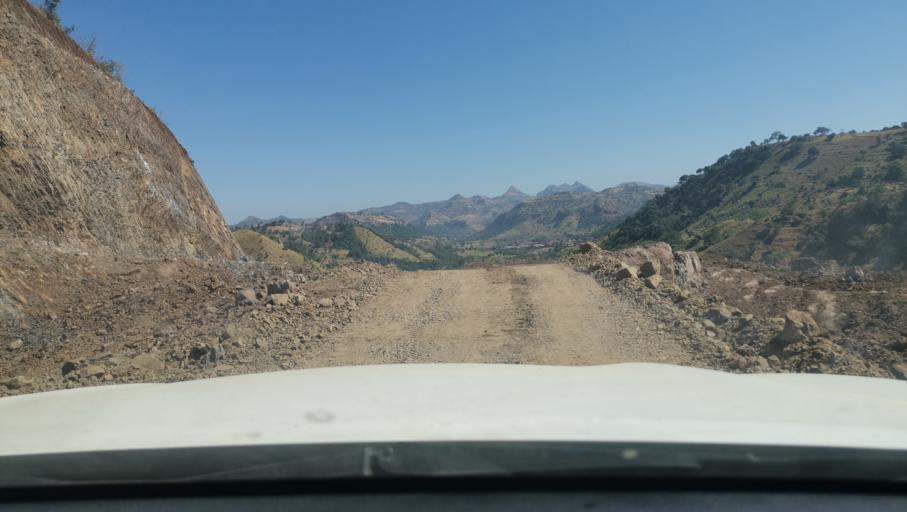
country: ET
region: Amhara
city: Debark'
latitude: 13.3048
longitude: 37.8314
